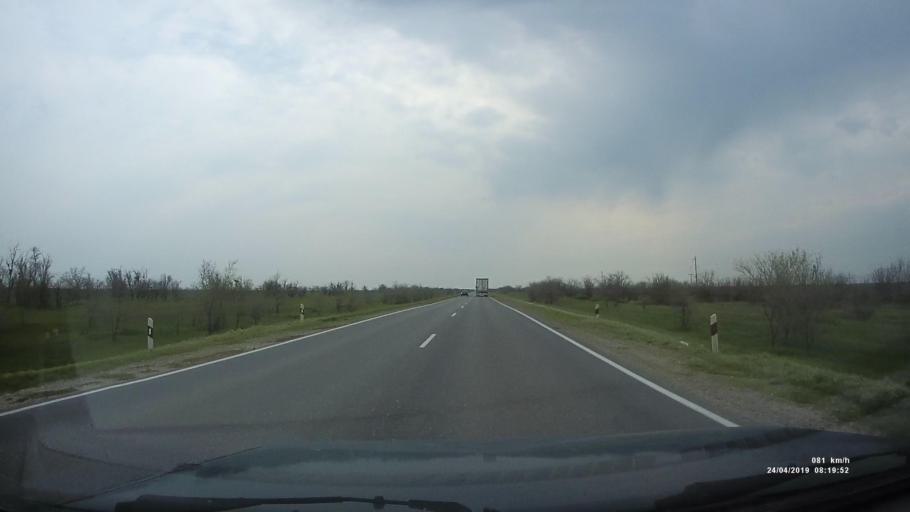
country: RU
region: Kalmykiya
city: Priyutnoye
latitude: 46.1056
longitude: 43.6728
